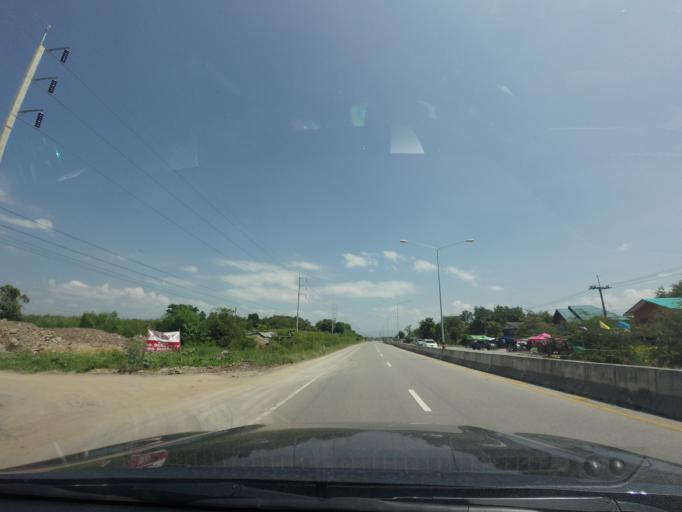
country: TH
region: Phetchabun
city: Lom Sak
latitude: 16.7671
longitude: 101.1615
